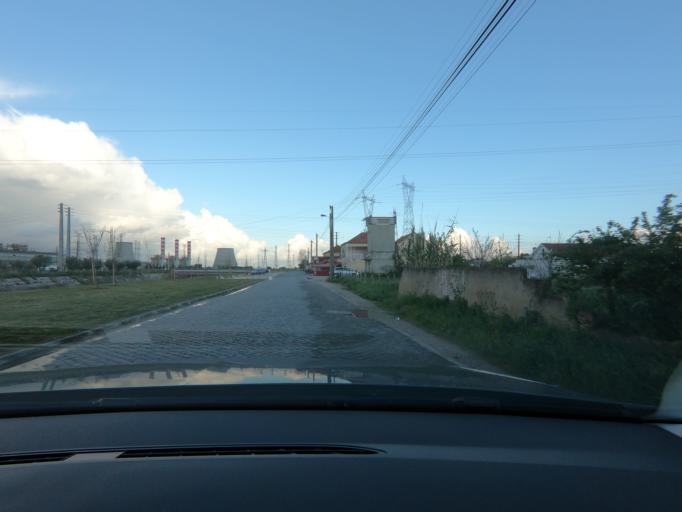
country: PT
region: Lisbon
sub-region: Alenquer
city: Carregado
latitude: 39.0117
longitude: -8.9629
